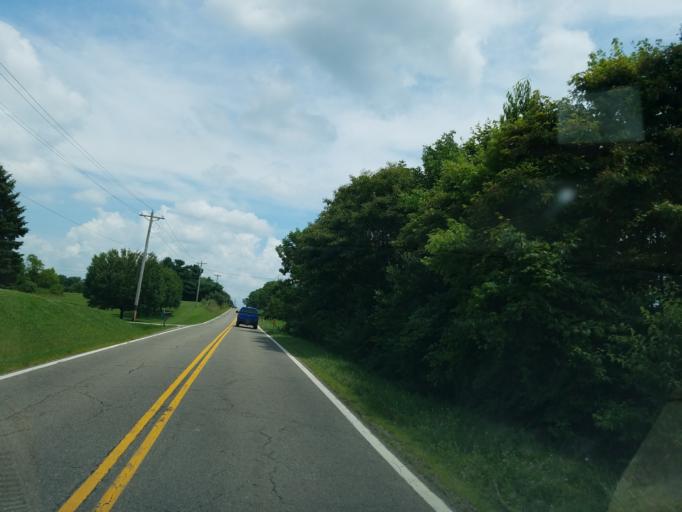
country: US
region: Ohio
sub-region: Licking County
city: Johnstown
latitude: 40.1571
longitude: -82.6229
